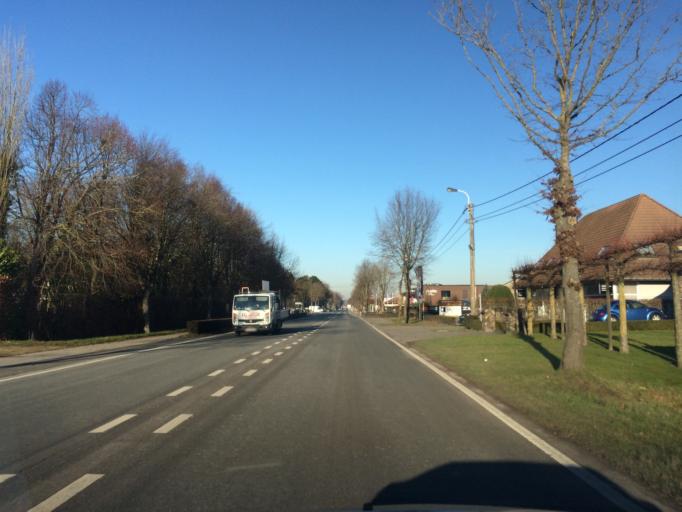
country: BE
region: Flanders
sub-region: Provincie West-Vlaanderen
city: Zedelgem
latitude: 51.1347
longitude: 3.1588
